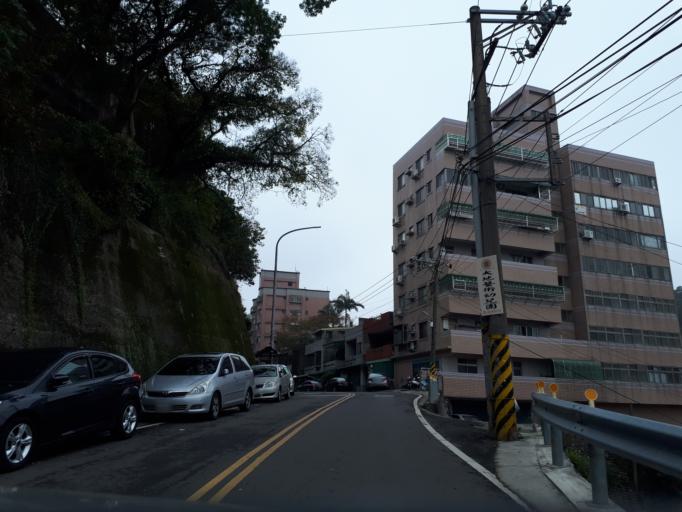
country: TW
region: Taiwan
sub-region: Hsinchu
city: Zhubei
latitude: 24.7344
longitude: 121.0840
